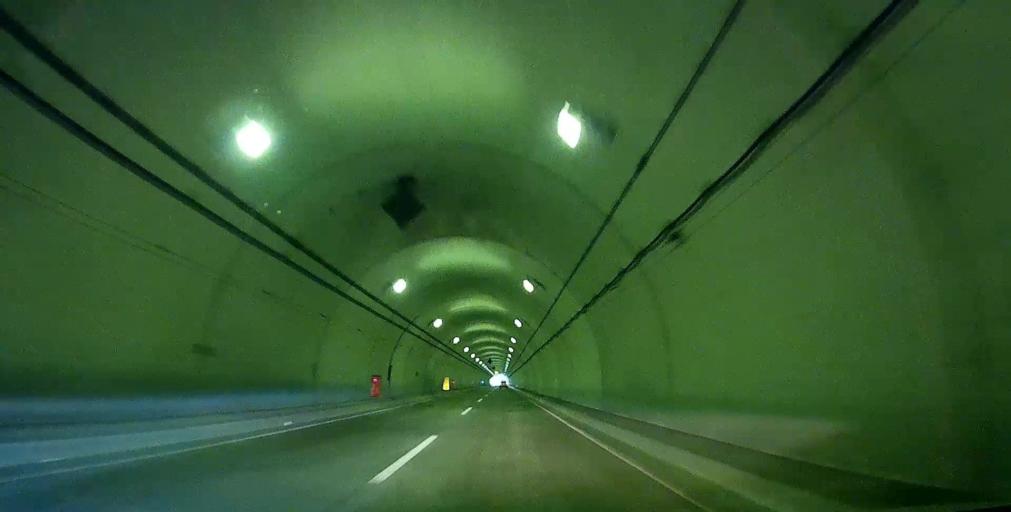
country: JP
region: Tokyo
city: Hachioji
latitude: 35.6270
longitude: 139.2689
